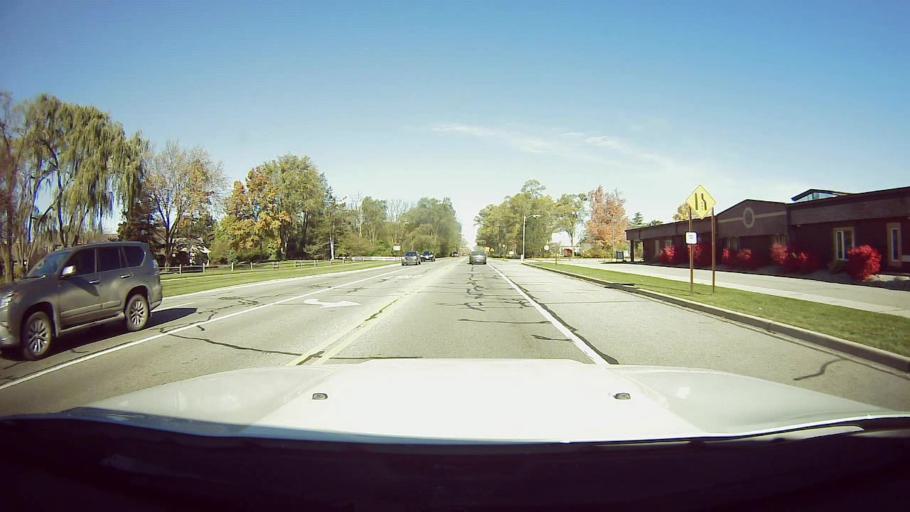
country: US
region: Michigan
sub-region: Oakland County
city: Farmington Hills
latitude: 42.5135
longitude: -83.3789
